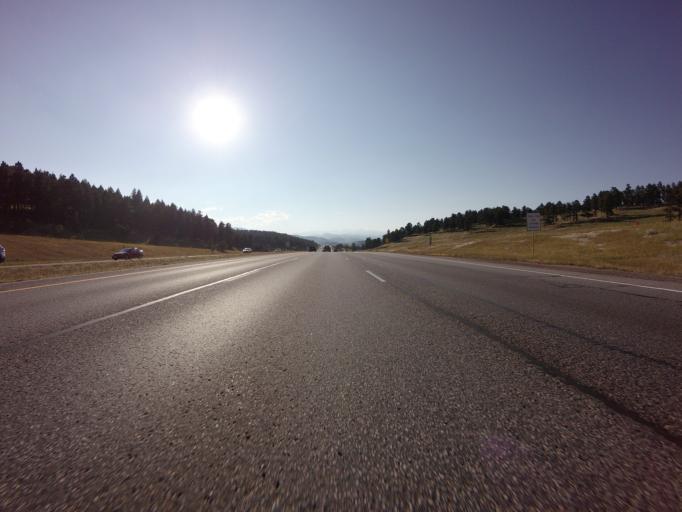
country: US
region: Colorado
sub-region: Jefferson County
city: Genesee
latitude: 39.7105
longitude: -105.2956
